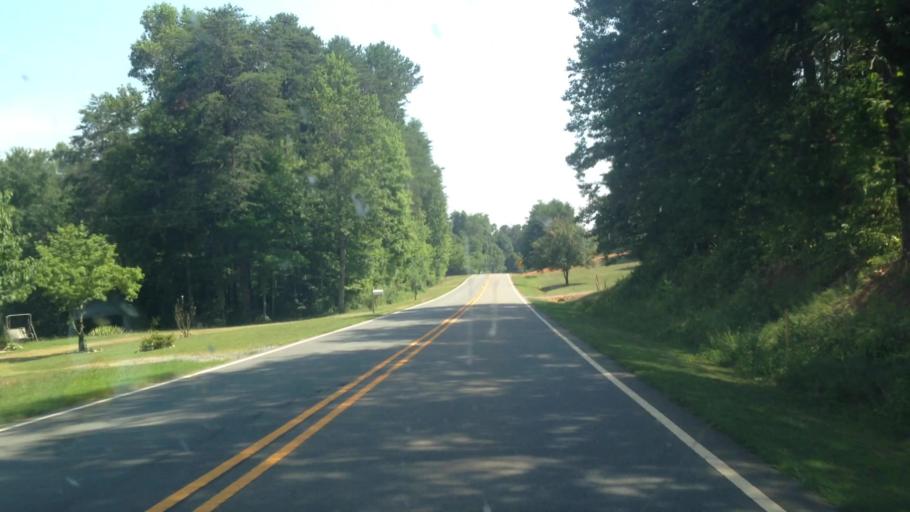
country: US
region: North Carolina
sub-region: Stokes County
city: Walnut Cove
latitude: 36.3918
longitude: -80.0951
